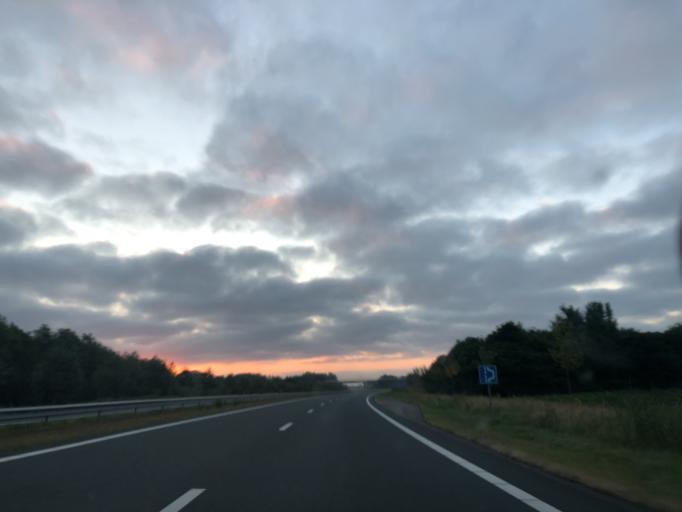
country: NL
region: Groningen
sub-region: Gemeente Veendam
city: Veendam
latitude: 53.0478
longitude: 6.8380
